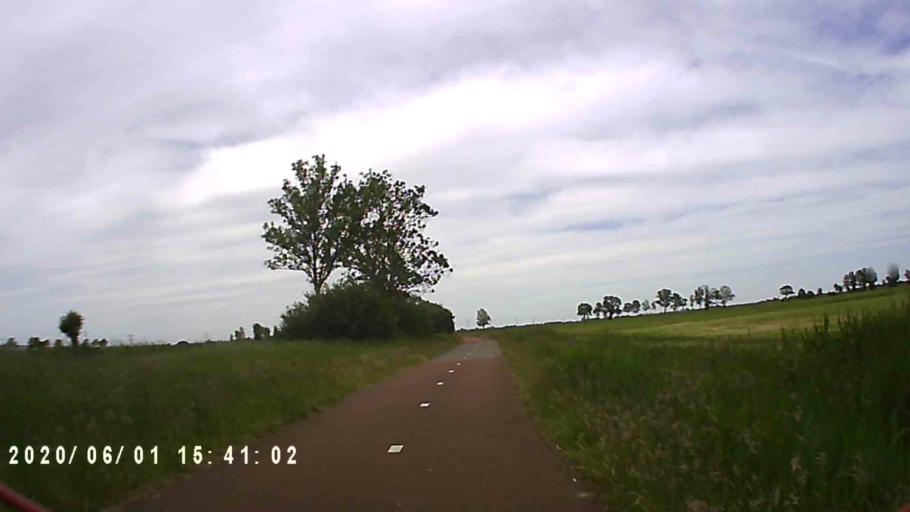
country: NL
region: Friesland
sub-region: Gemeente Boarnsterhim
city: Wergea
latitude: 53.1550
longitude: 5.8237
